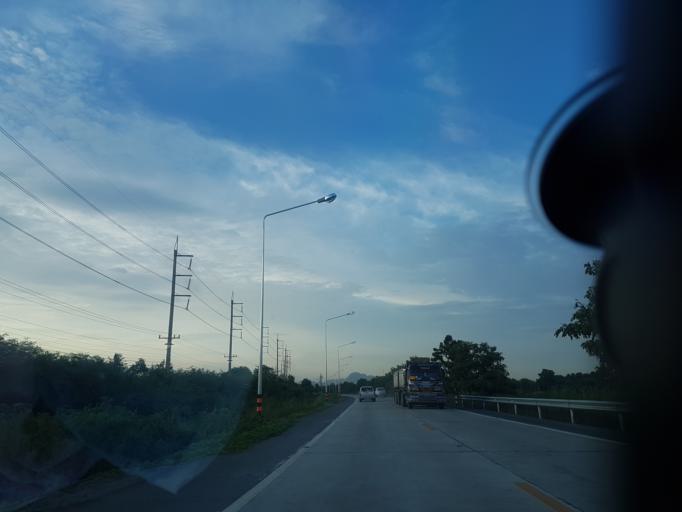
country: TH
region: Phra Nakhon Si Ayutthaya
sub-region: Amphoe Tha Ruea
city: Tha Ruea
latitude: 14.5468
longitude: 100.7611
